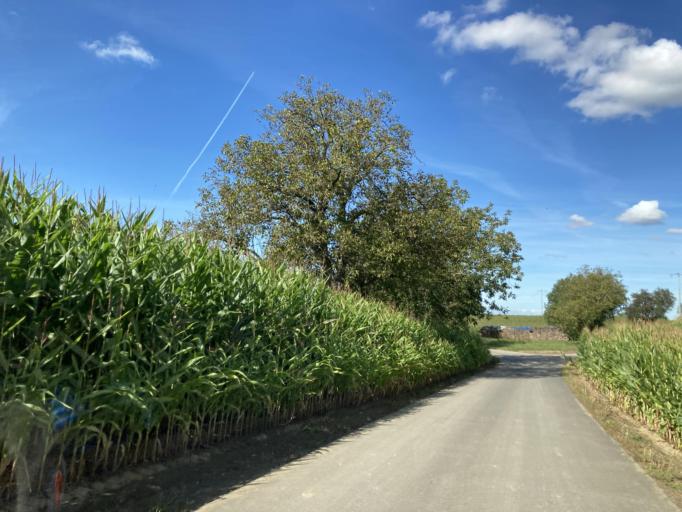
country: DE
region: Baden-Wuerttemberg
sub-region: Freiburg Region
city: Mullheim
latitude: 47.8119
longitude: 7.6475
